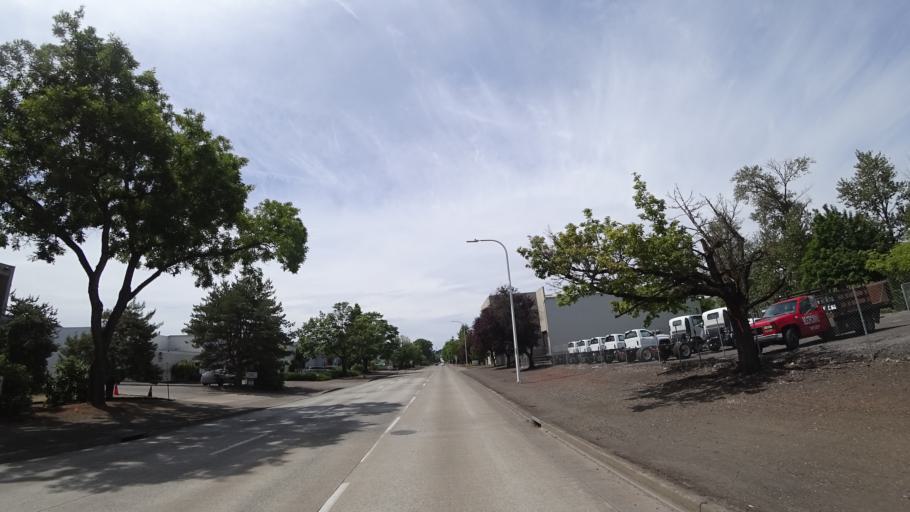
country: US
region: Oregon
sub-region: Multnomah County
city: Portland
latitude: 45.5605
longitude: -122.7079
